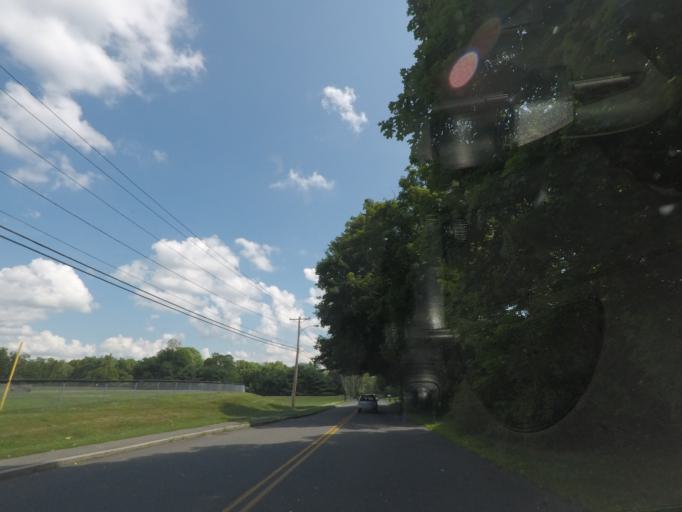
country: US
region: Massachusetts
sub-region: Hampden County
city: Monson
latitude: 42.1123
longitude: -72.3265
